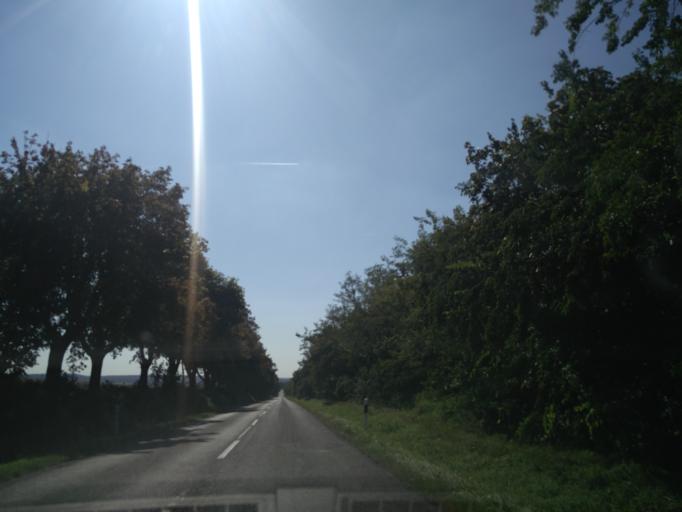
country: HU
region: Fejer
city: Lovasbereny
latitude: 47.3184
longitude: 18.5674
